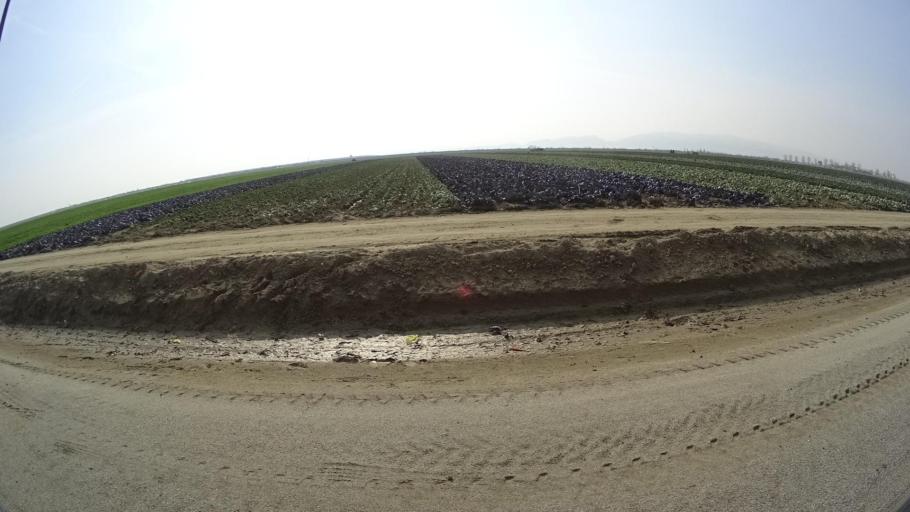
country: US
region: California
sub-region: Kern County
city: Weedpatch
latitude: 35.0752
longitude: -118.9461
